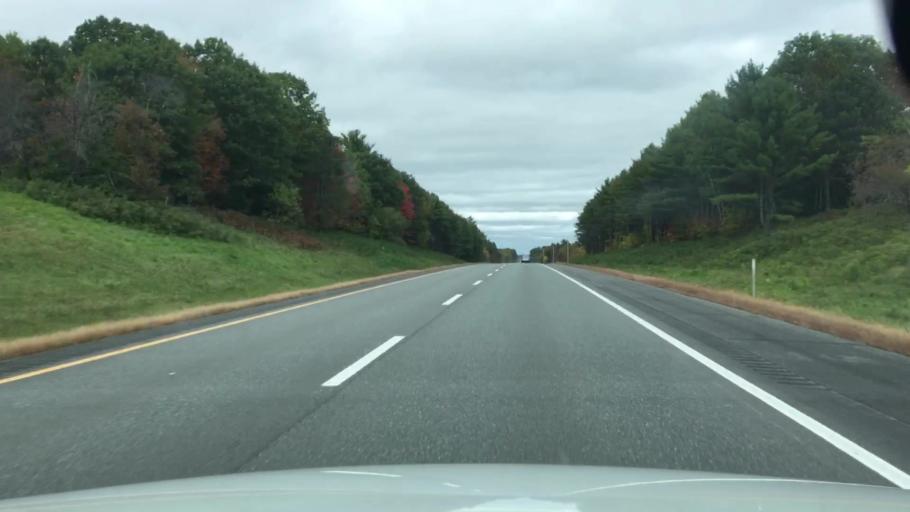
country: US
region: Maine
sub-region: Waldo County
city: Burnham
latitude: 44.7451
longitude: -69.4258
